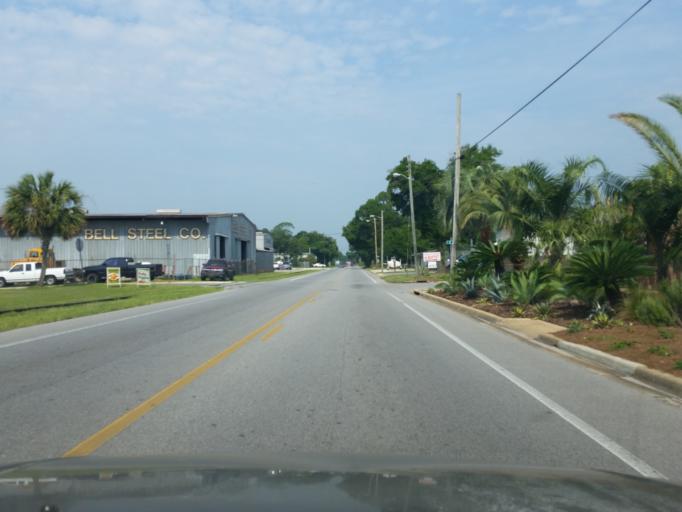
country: US
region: Florida
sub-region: Escambia County
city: Pensacola
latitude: 30.4054
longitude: -87.2271
